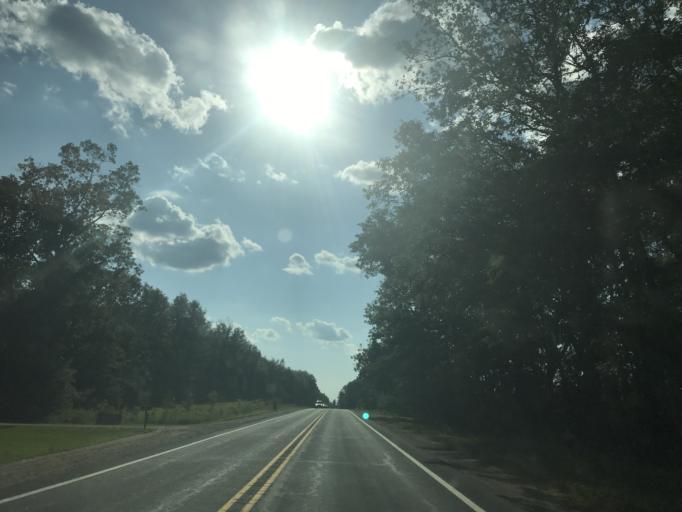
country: US
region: Michigan
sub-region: Newaygo County
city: White Cloud
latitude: 43.5683
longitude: -85.7959
